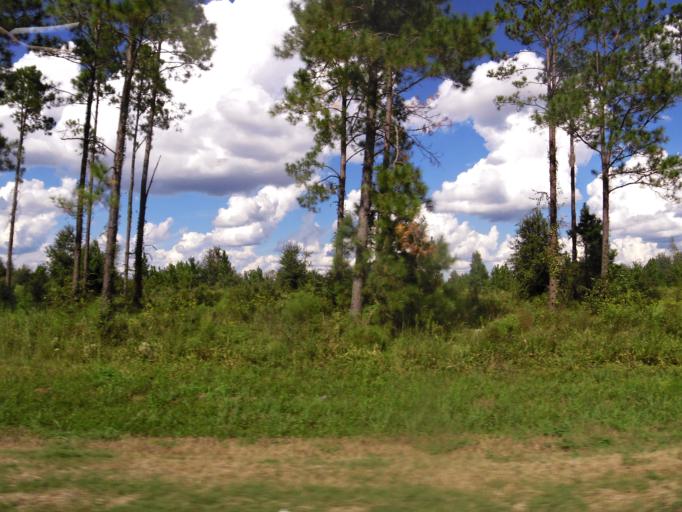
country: US
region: Georgia
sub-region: Lowndes County
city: Valdosta
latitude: 30.8052
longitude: -83.2064
